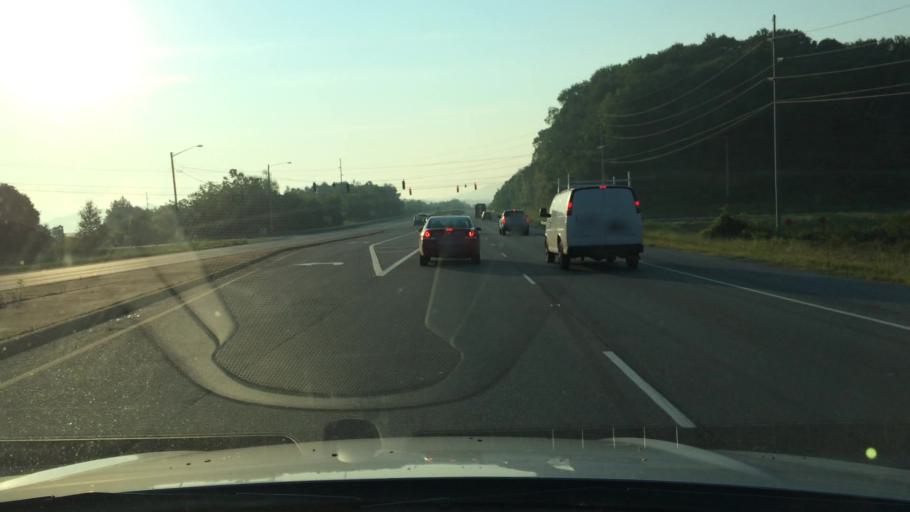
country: US
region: Tennessee
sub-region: Giles County
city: Pulaski
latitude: 35.1703
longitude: -87.0528
